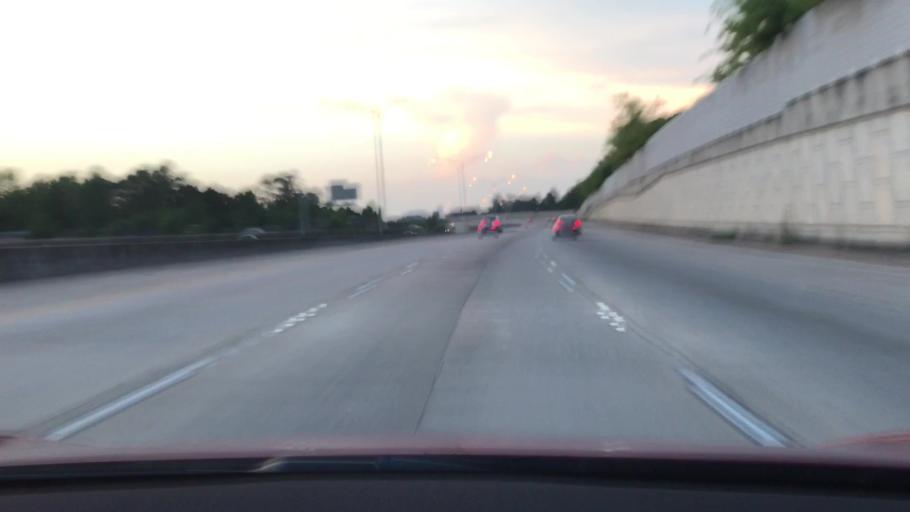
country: US
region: Louisiana
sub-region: Bossier Parish
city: Bossier City
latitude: 32.4630
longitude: -93.7564
